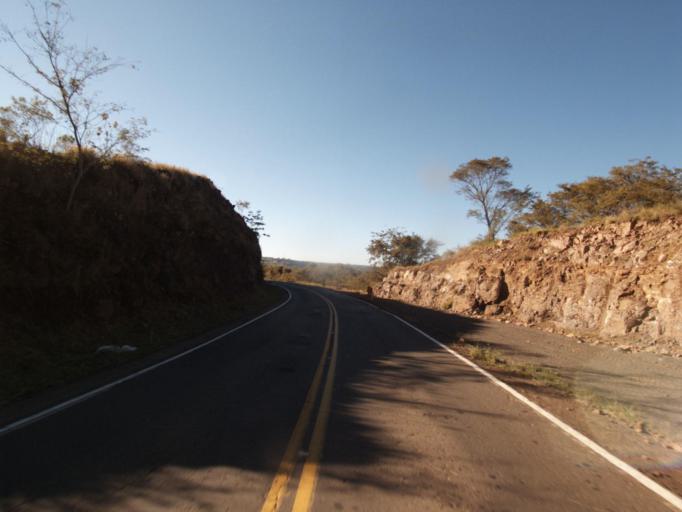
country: AR
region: Misiones
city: Bernardo de Irigoyen
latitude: -26.4953
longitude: -53.5017
